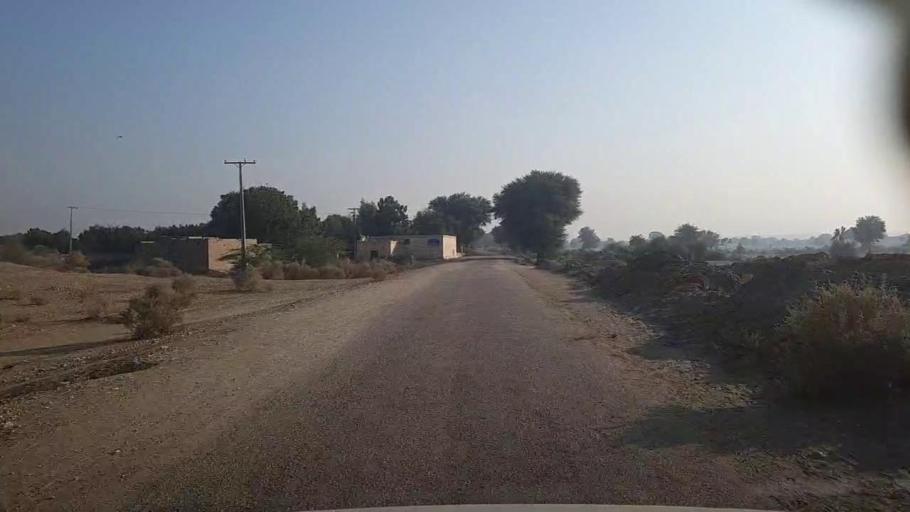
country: PK
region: Sindh
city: Karaundi
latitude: 26.7615
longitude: 68.4757
